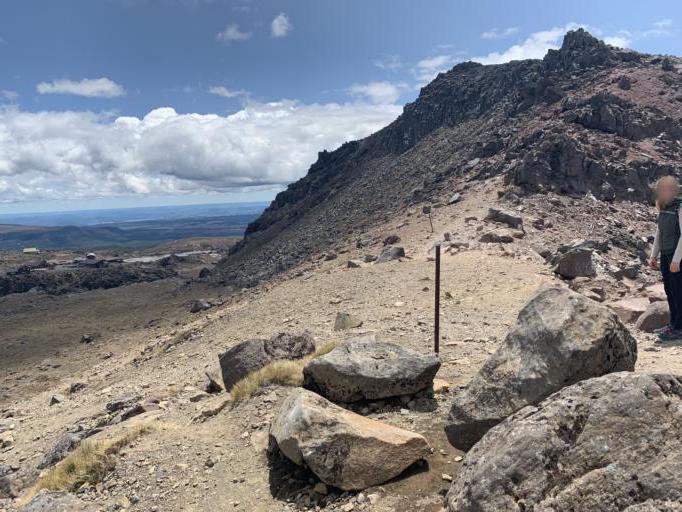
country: NZ
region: Manawatu-Wanganui
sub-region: Ruapehu District
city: Waiouru
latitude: -39.2360
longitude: 175.5613
